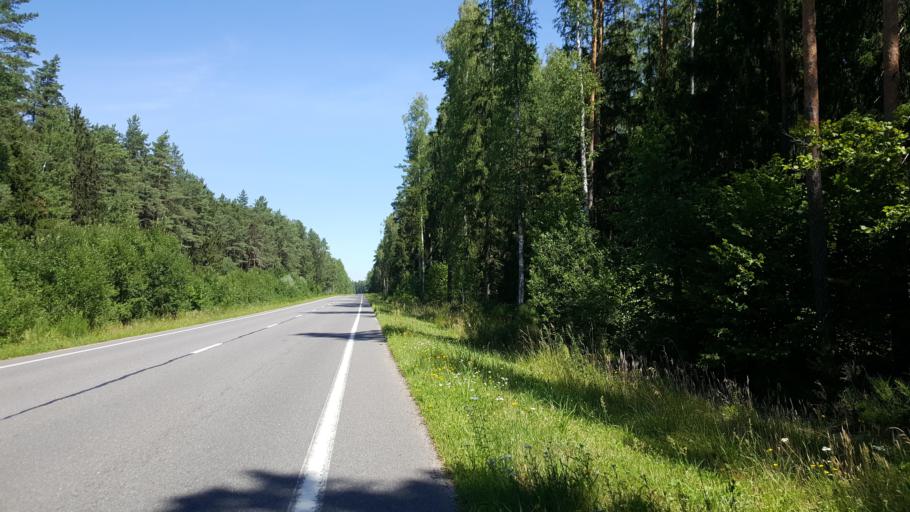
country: BY
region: Brest
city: Pruzhany
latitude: 52.5045
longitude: 24.1763
